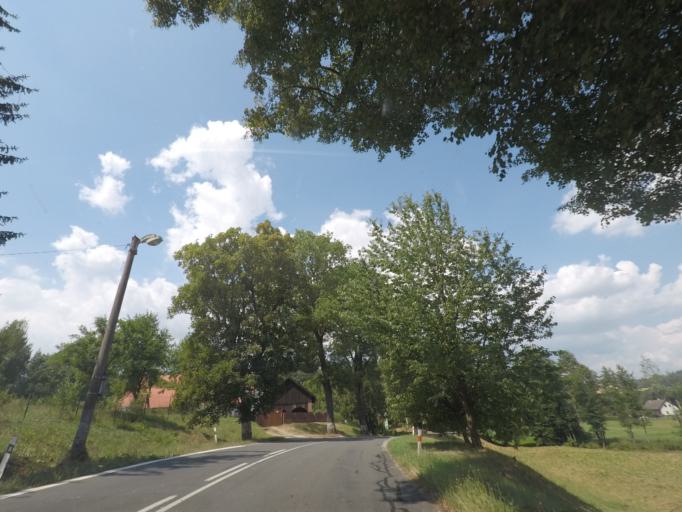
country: CZ
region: Kralovehradecky
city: Zadni Mostek
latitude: 50.5292
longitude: 15.6795
